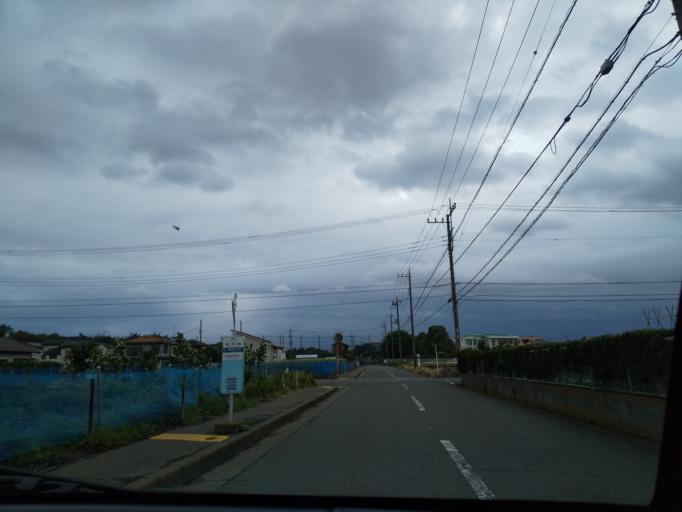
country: JP
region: Kanagawa
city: Minami-rinkan
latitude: 35.4297
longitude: 139.4422
